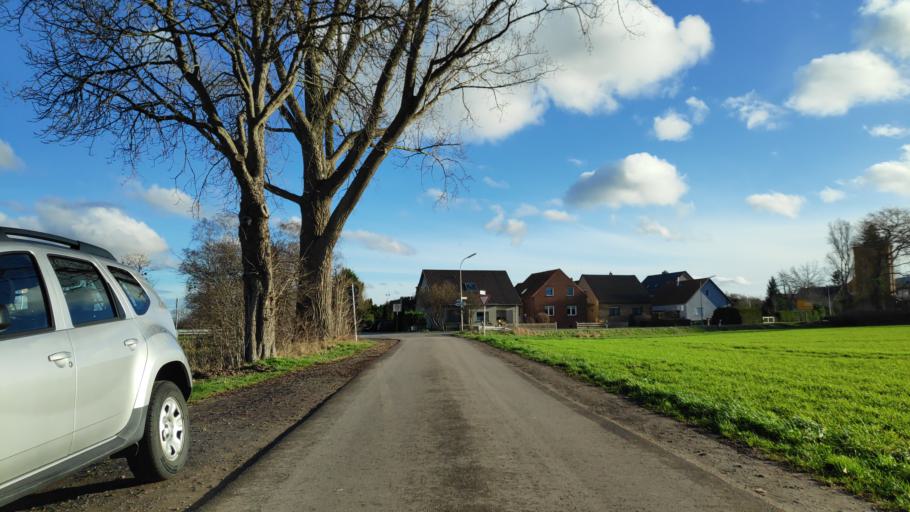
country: DE
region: North Rhine-Westphalia
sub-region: Regierungsbezirk Detmold
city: Minden
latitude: 52.2750
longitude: 8.8624
